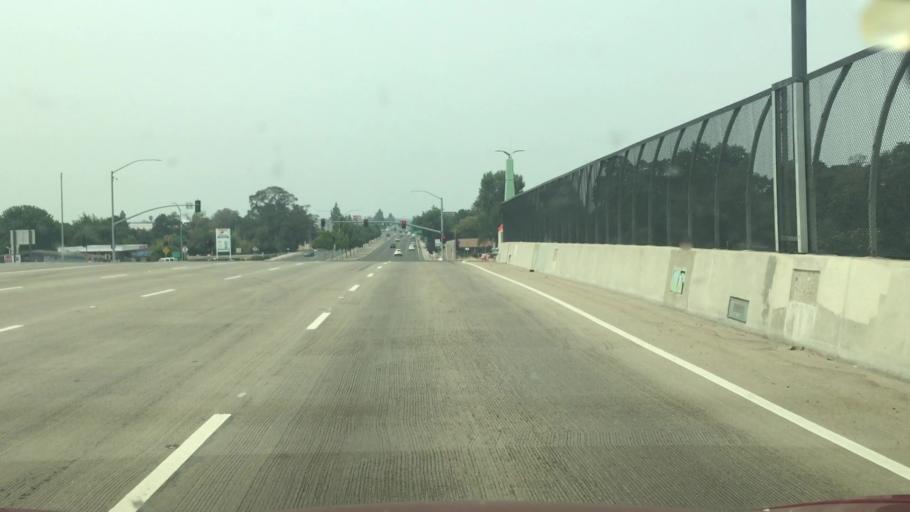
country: US
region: California
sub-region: San Joaquin County
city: Morada
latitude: 38.0214
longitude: -121.2583
